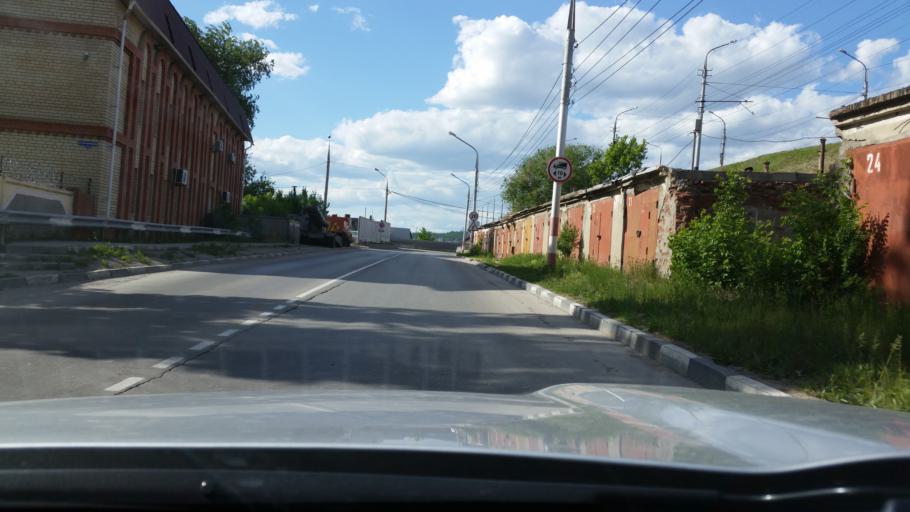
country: RU
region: Saratov
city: Engel's
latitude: 51.5048
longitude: 46.0782
